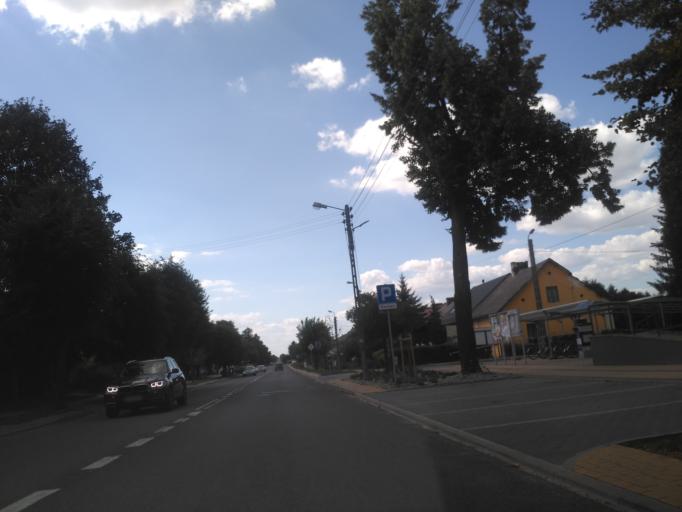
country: PL
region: Lublin Voivodeship
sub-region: Powiat swidnicki
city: Piaski
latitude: 51.1391
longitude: 22.8470
